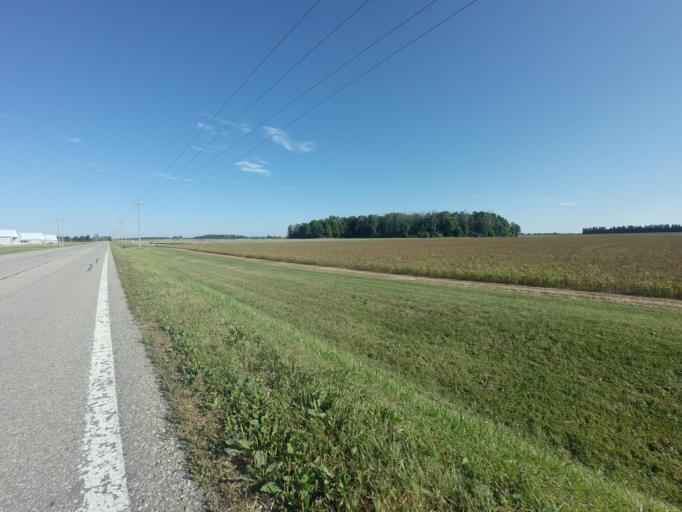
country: CA
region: Ontario
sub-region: Wellington County
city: Guelph
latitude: 43.6445
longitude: -80.4075
